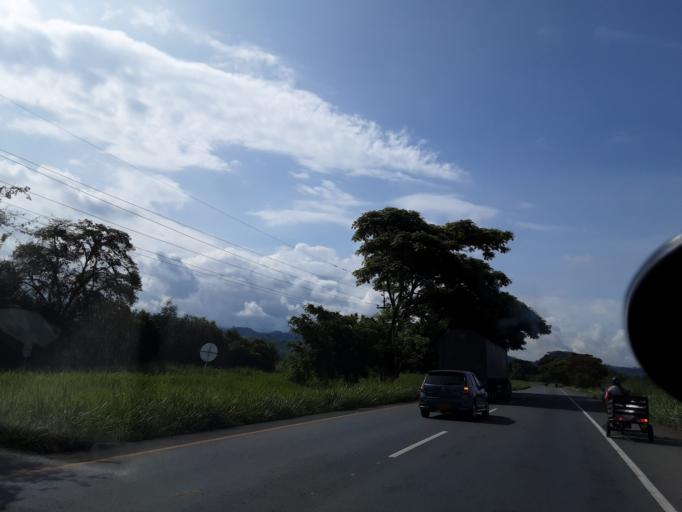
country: CO
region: Valle del Cauca
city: Buga
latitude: 3.8681
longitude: -76.3037
